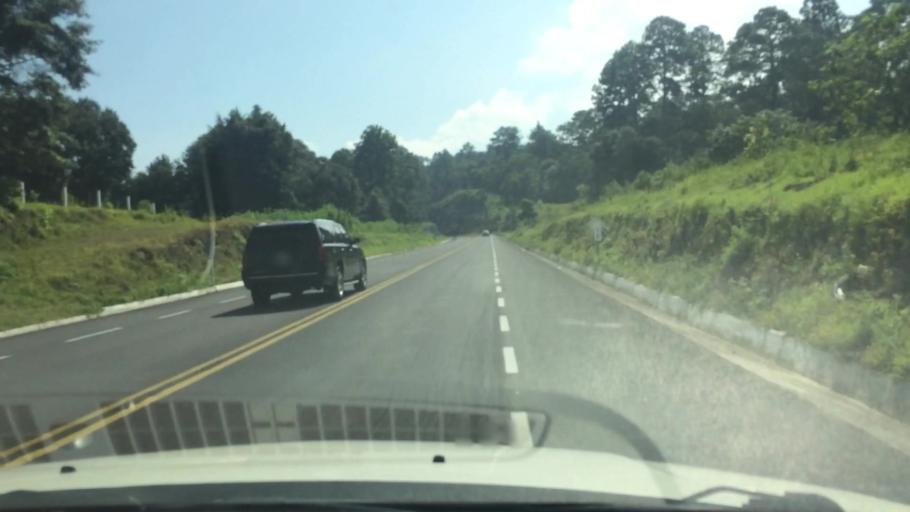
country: MX
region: Mexico
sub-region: Amanalco
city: Polvillos (San Bartolo Quinta Seccion)
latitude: 19.2198
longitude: -100.0928
